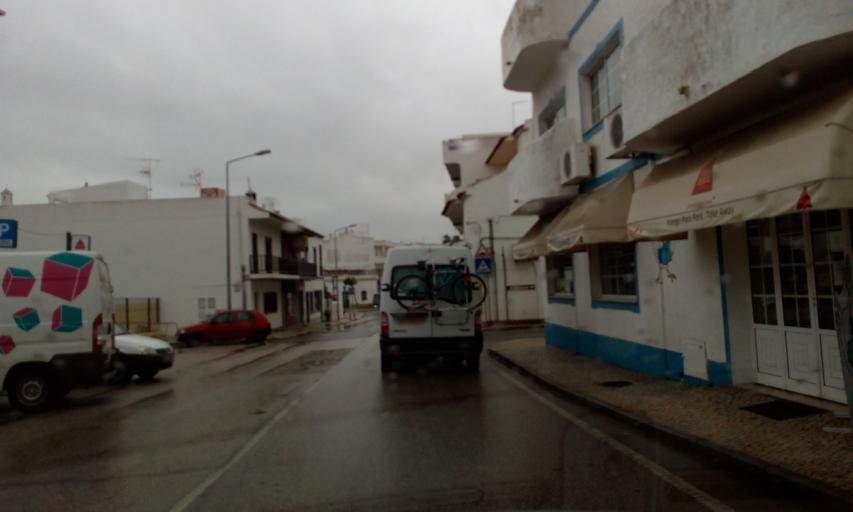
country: PT
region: Faro
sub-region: Albufeira
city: Guia
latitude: 37.1276
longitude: -8.3011
